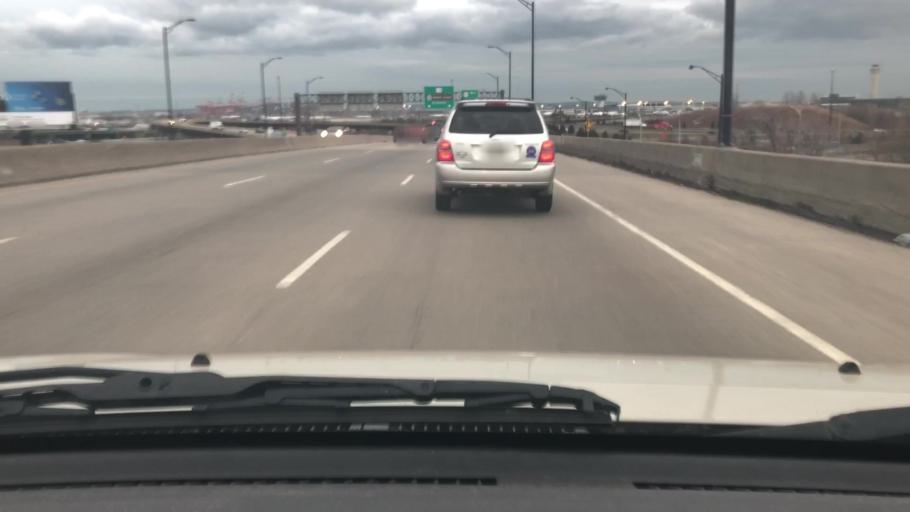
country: US
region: New Jersey
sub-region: Essex County
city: Newark
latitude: 40.7116
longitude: -74.1833
